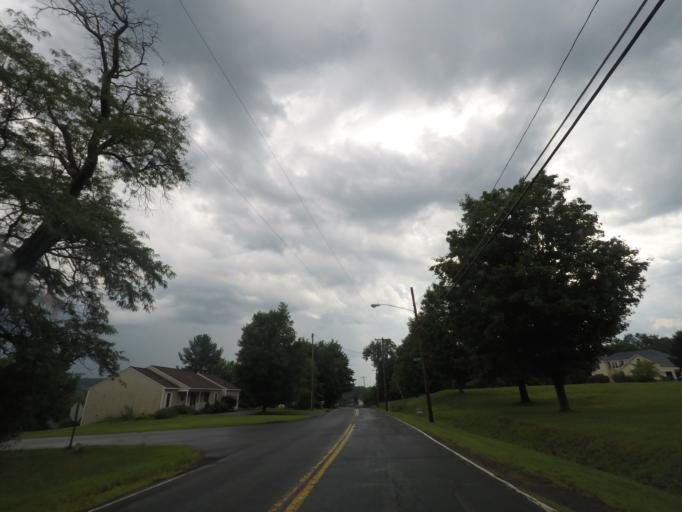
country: US
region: New York
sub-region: Rensselaer County
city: Poestenkill
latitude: 42.7368
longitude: -73.5976
